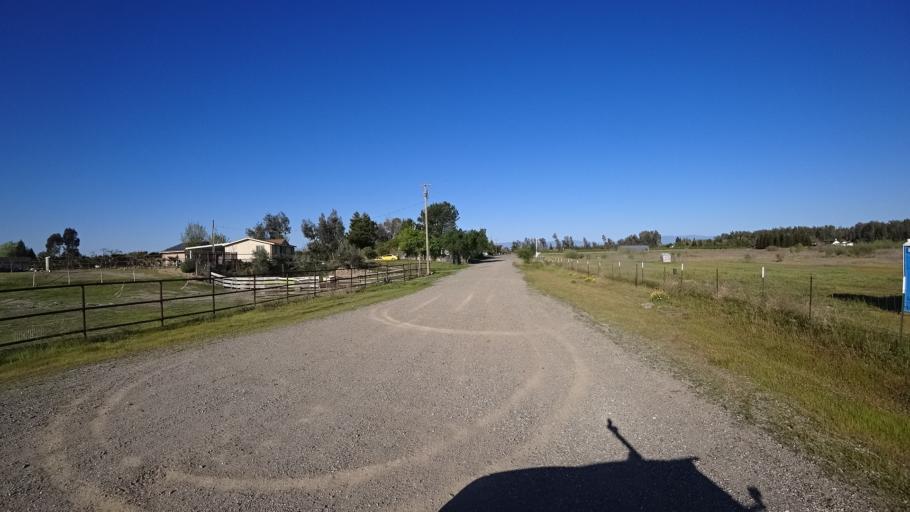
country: US
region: California
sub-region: Glenn County
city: Orland
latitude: 39.7583
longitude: -122.2064
